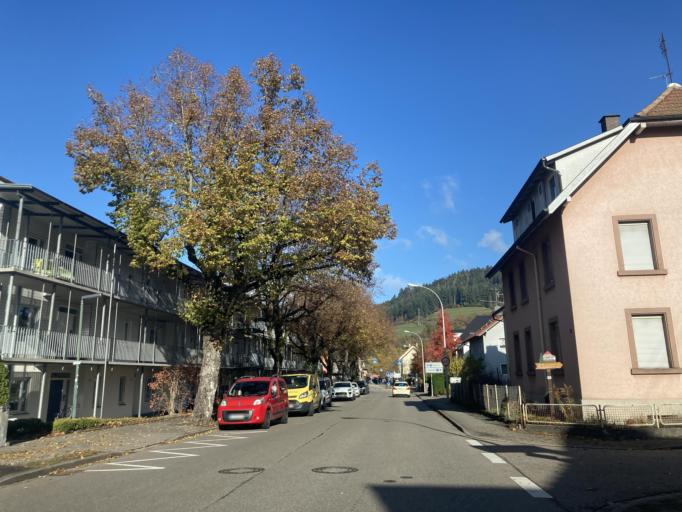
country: DE
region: Baden-Wuerttemberg
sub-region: Freiburg Region
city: Hofstetten
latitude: 48.2752
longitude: 8.0903
